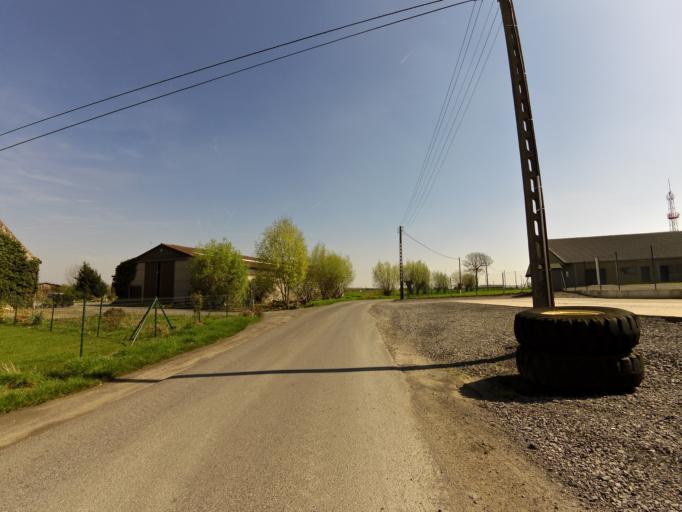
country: BE
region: Flanders
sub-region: Provincie West-Vlaanderen
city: Ichtegem
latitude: 51.0796
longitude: 3.0057
